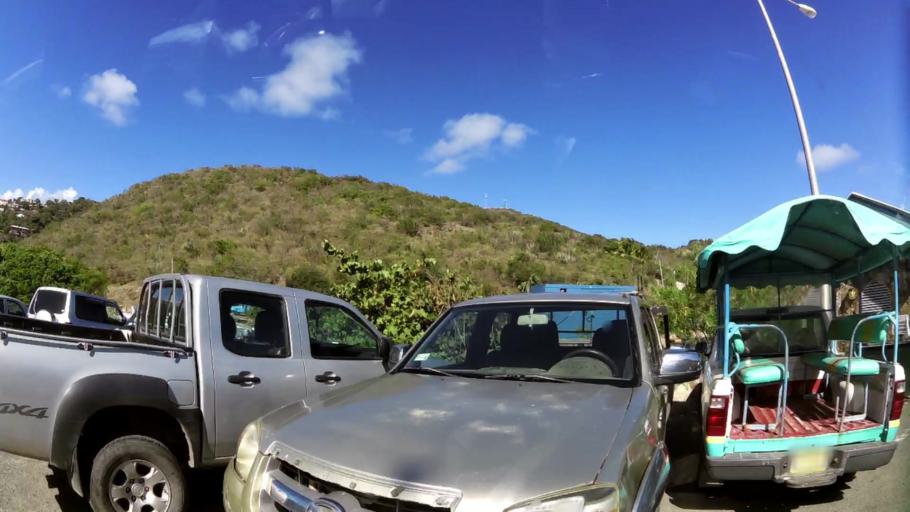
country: VG
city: Tortola
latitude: 18.4893
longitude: -64.3823
